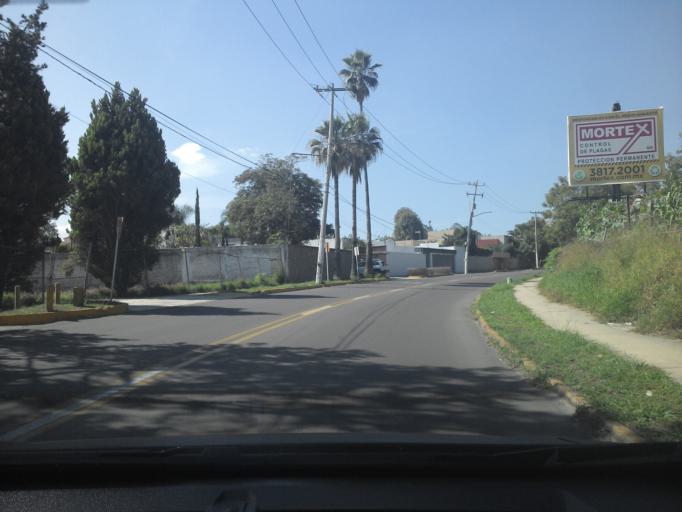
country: MX
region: Jalisco
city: Zapopan2
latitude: 20.6920
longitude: -103.4058
